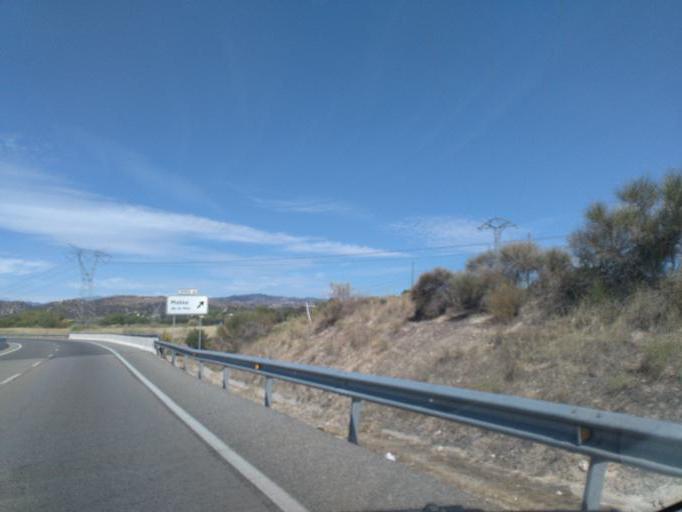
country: ES
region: Madrid
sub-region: Provincia de Madrid
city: Villanueva del Pardillo
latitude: 40.5202
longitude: -3.9378
